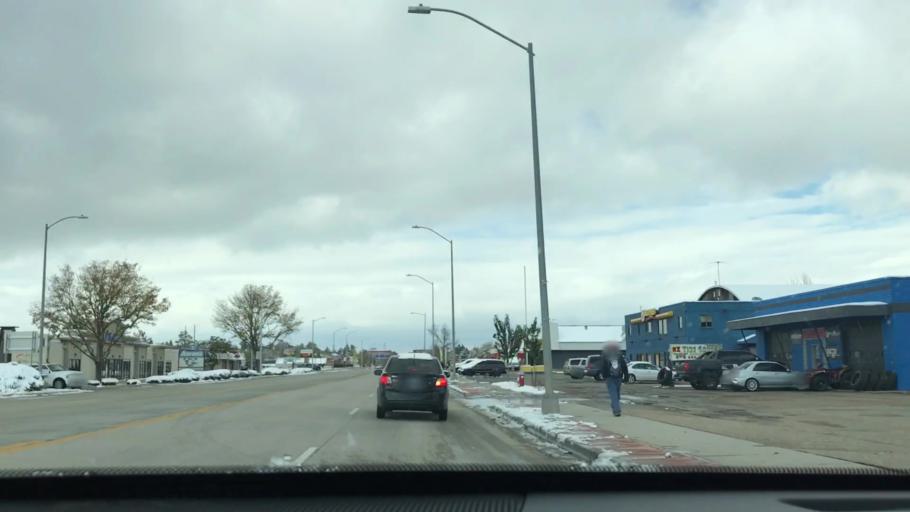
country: US
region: Colorado
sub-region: Boulder County
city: Longmont
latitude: 40.1533
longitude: -105.1025
